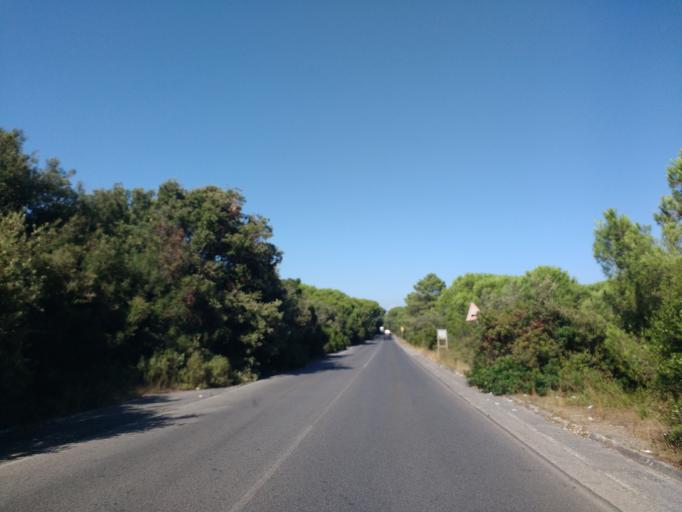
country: IT
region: Latium
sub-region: Citta metropolitana di Roma Capitale
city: Acilia-Castel Fusano-Ostia Antica
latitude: 41.7034
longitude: 12.3483
